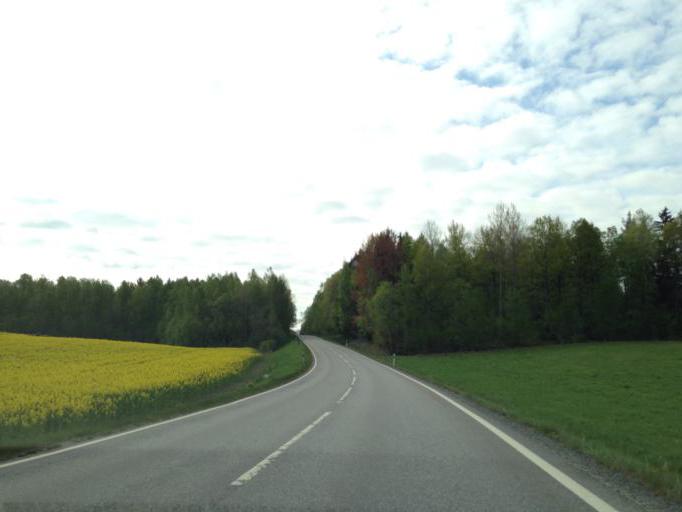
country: SE
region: Soedermanland
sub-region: Flens Kommun
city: Malmkoping
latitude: 59.0799
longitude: 16.8090
